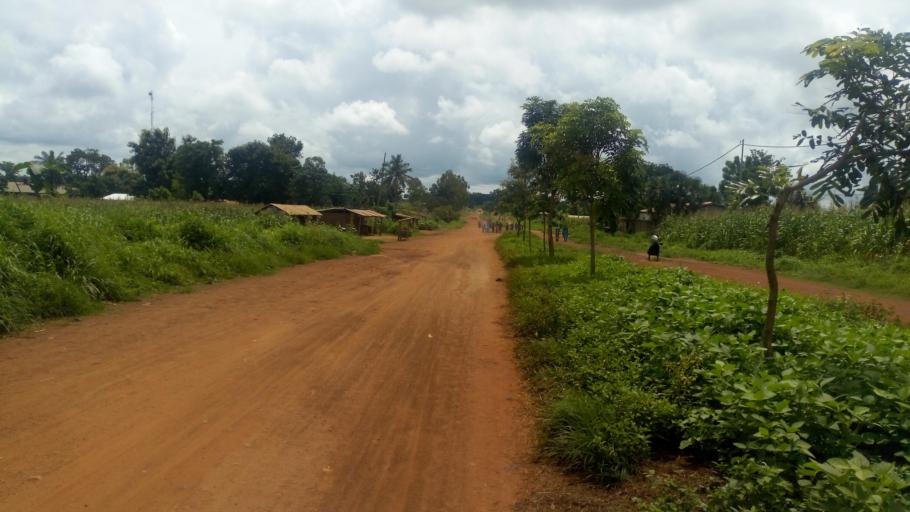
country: TG
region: Centrale
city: Sotouboua
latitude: 8.5553
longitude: 0.9889
